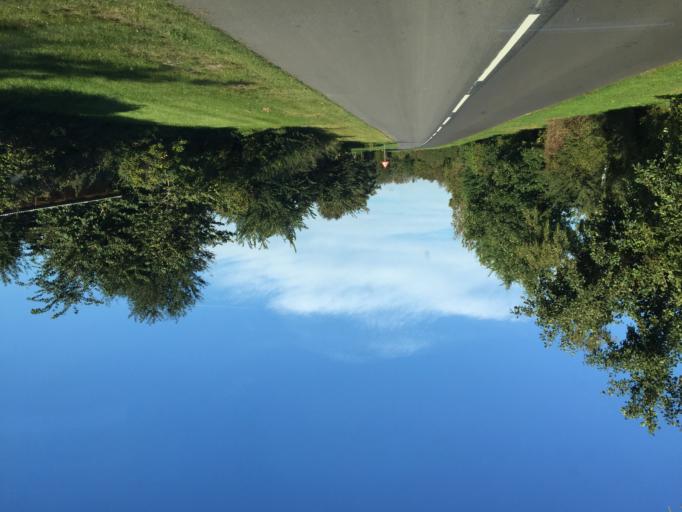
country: DK
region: Zealand
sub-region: Odsherred Kommune
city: Hojby
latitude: 55.9028
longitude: 11.5544
